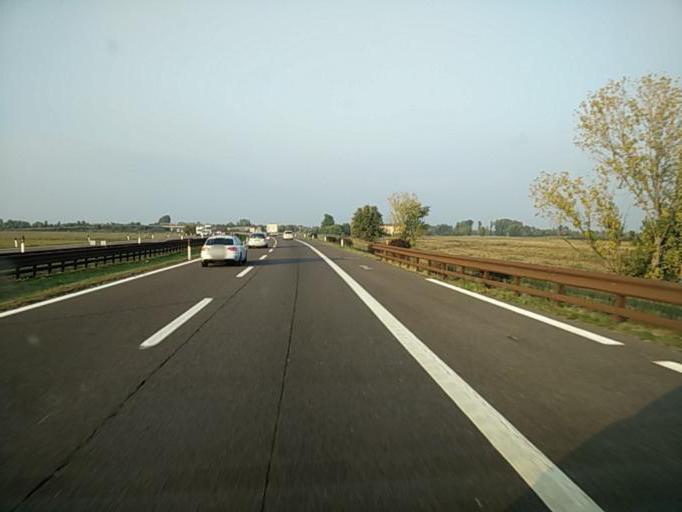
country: IT
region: Veneto
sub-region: Provincia di Verona
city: Vigasio
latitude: 45.3251
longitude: 10.9160
